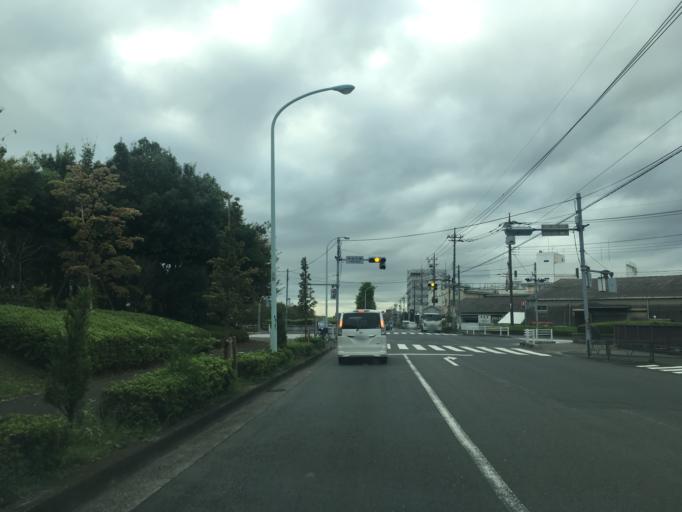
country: JP
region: Tokyo
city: Fussa
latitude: 35.7447
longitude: 139.3829
